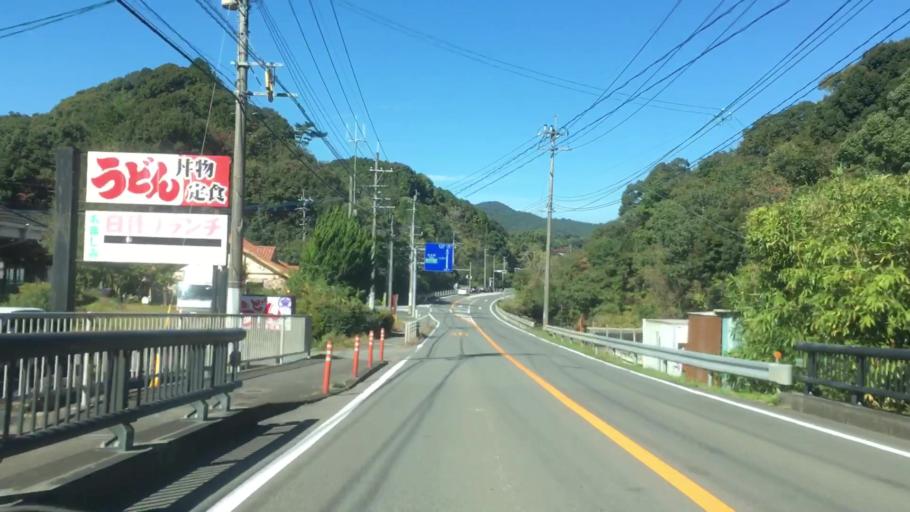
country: JP
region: Nagasaki
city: Sasebo
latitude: 32.9943
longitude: 129.7333
